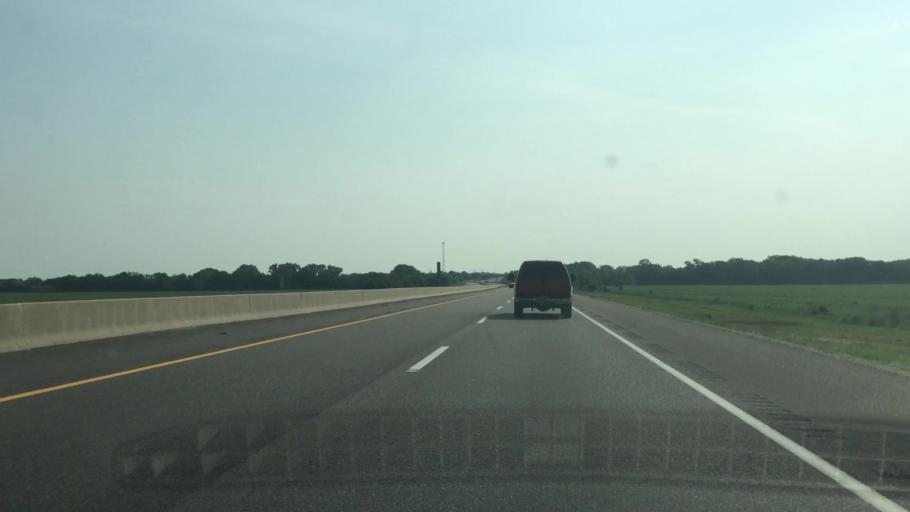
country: US
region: Kansas
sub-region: Butler County
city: Towanda
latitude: 37.7558
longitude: -97.0142
